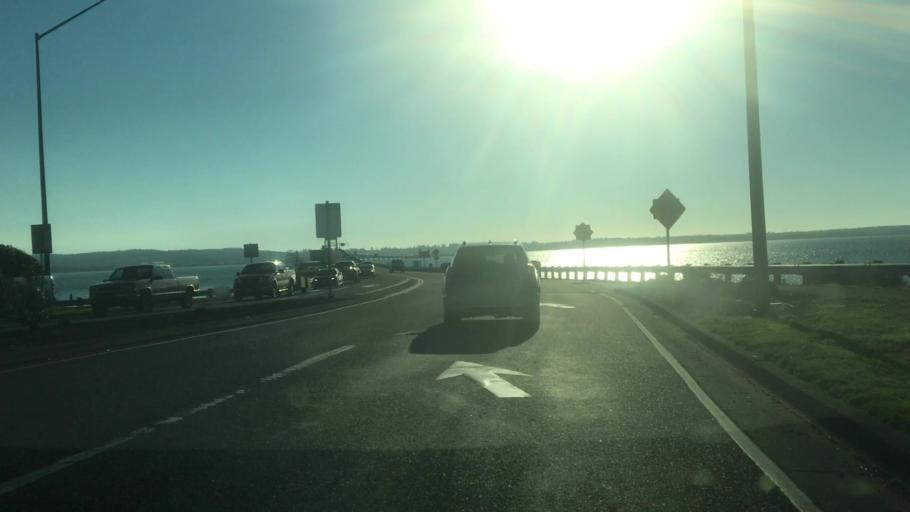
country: US
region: Oregon
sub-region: Clatsop County
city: Astoria
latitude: 46.1828
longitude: -123.8613
